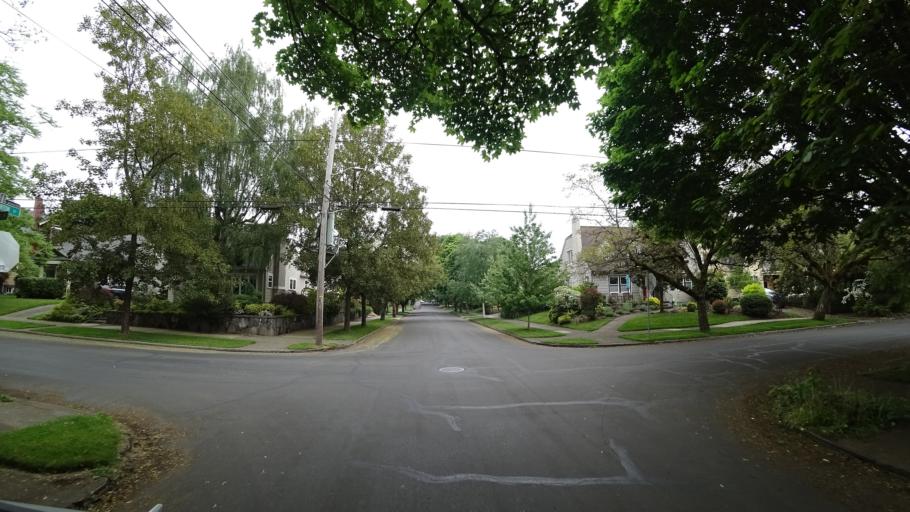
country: US
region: Oregon
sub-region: Multnomah County
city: Portland
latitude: 45.5437
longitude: -122.6545
